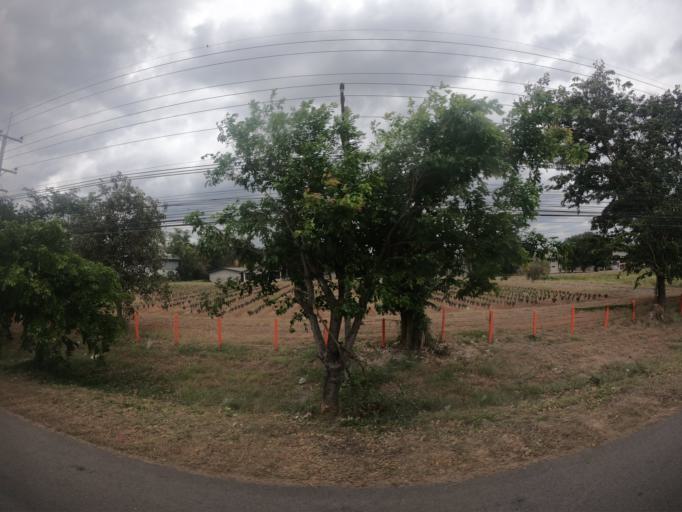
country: TH
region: Nakhon Ratchasima
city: Nakhon Ratchasima
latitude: 14.8748
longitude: 102.1780
